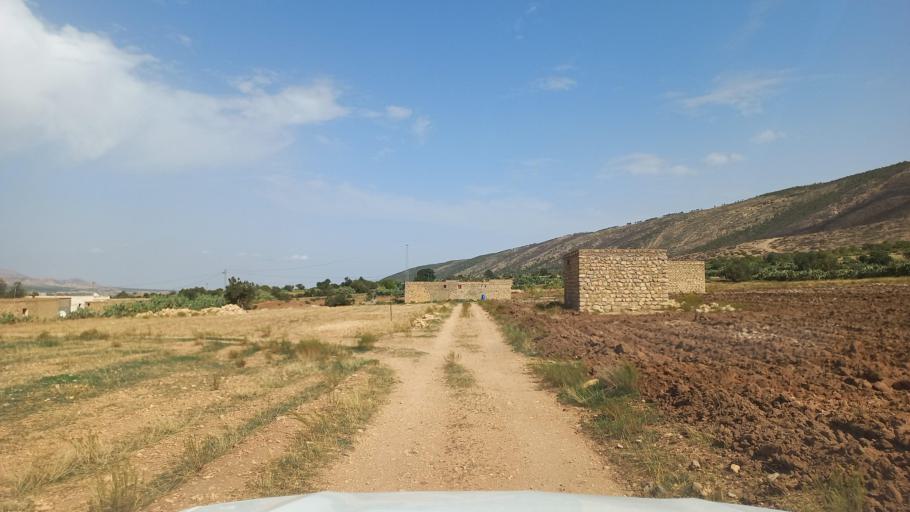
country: TN
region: Al Qasrayn
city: Kasserine
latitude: 35.3566
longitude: 8.8899
